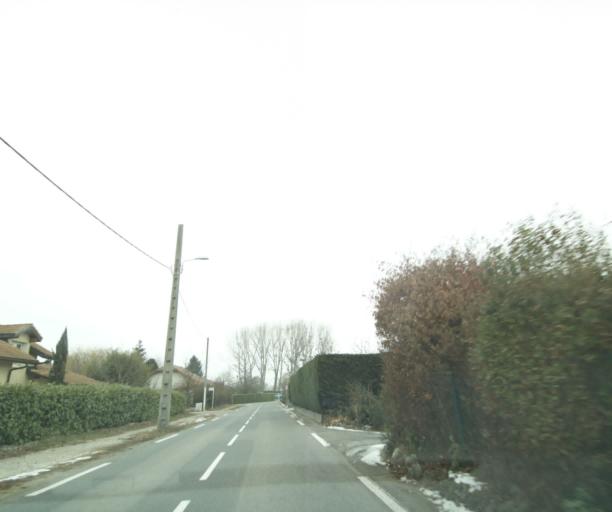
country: FR
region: Rhone-Alpes
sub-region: Departement de la Haute-Savoie
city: Reignier-Esery
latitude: 46.1345
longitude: 6.2845
